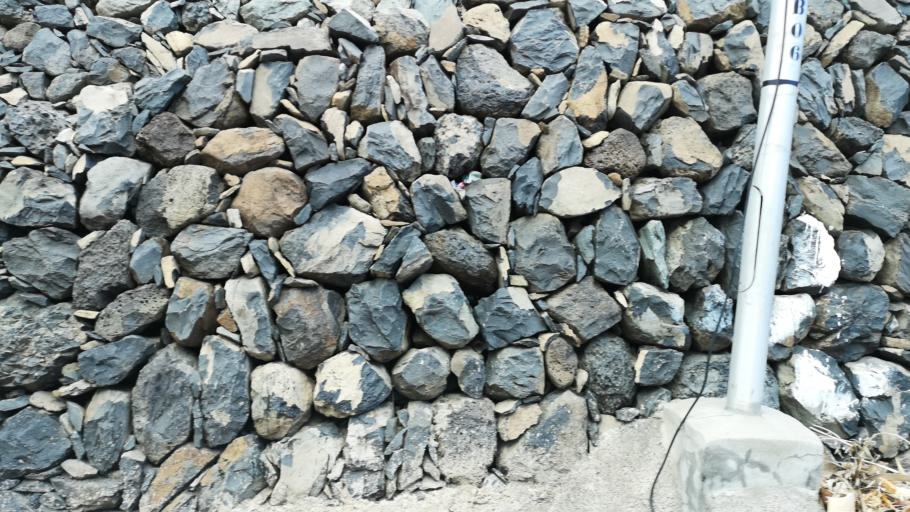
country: ES
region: Canary Islands
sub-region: Provincia de Santa Cruz de Tenerife
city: Hermigua
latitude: 28.1759
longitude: -17.1863
